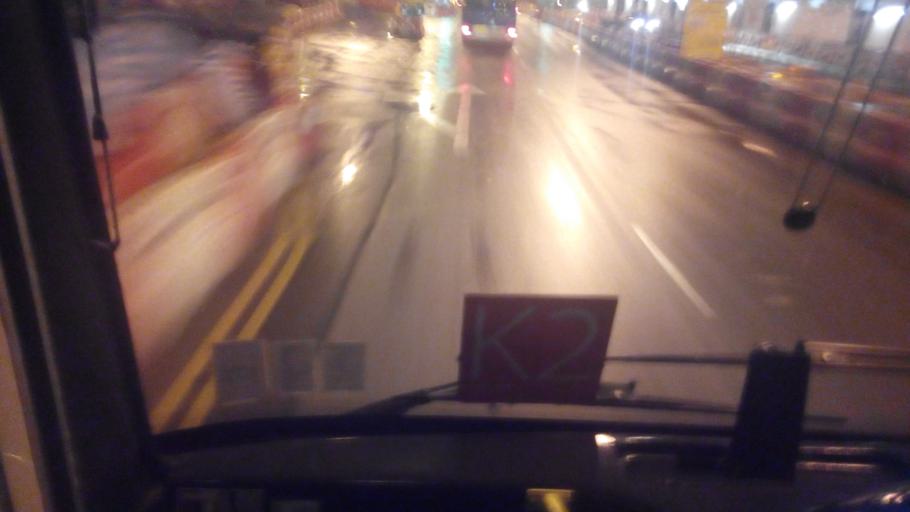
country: HK
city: Hong Kong
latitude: 22.3022
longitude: 114.1624
